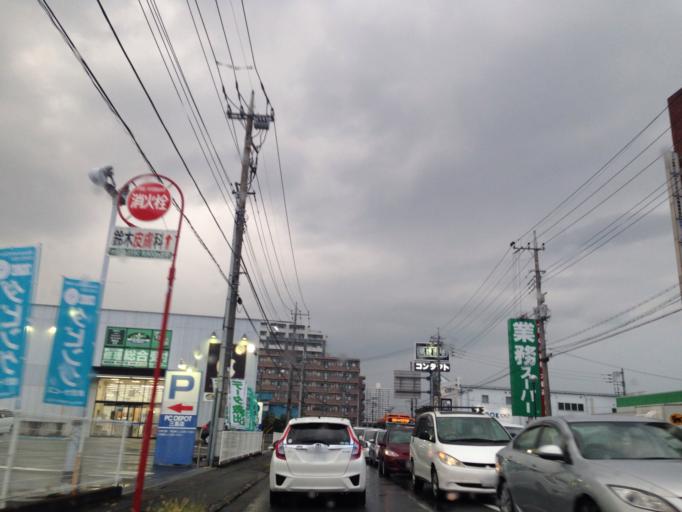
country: JP
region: Shizuoka
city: Mishima
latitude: 35.1104
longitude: 138.9150
